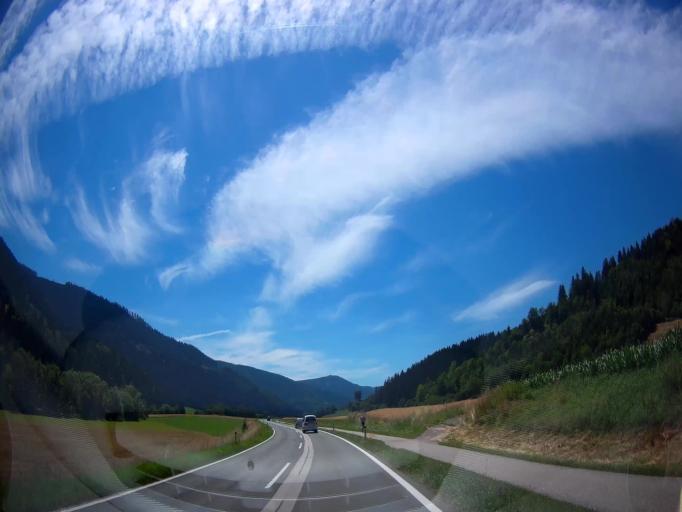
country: AT
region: Carinthia
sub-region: Politischer Bezirk Sankt Veit an der Glan
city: Strassburg
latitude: 46.8915
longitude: 14.3199
